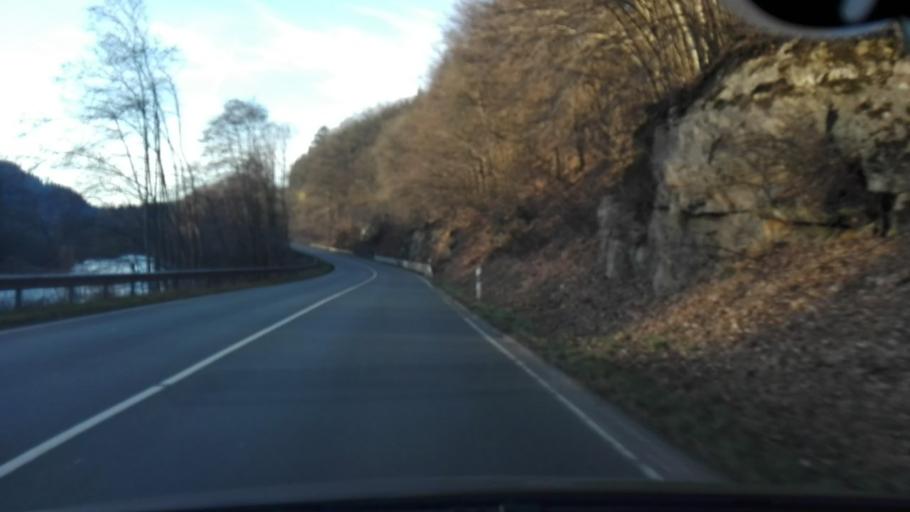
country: DE
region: North Rhine-Westphalia
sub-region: Regierungsbezirk Arnsberg
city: Finnentrop
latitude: 51.2083
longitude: 7.9737
